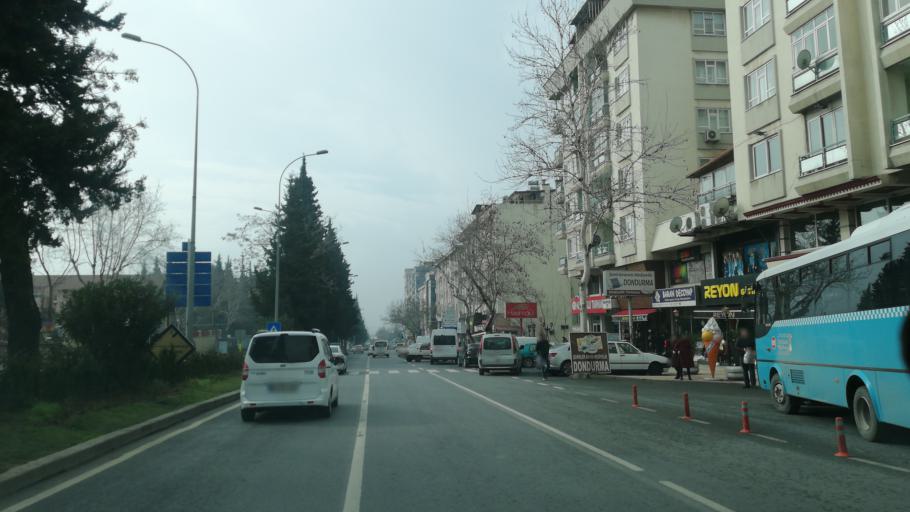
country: TR
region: Kahramanmaras
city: Kahramanmaras
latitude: 37.5741
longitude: 36.9259
